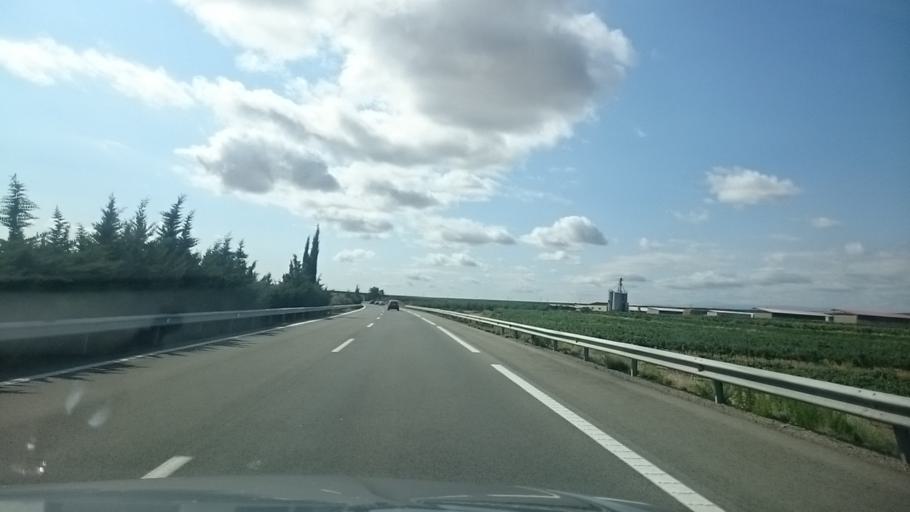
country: ES
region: La Rioja
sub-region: Provincia de La Rioja
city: Aldeanueva de Ebro
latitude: 42.2215
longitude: -1.8952
